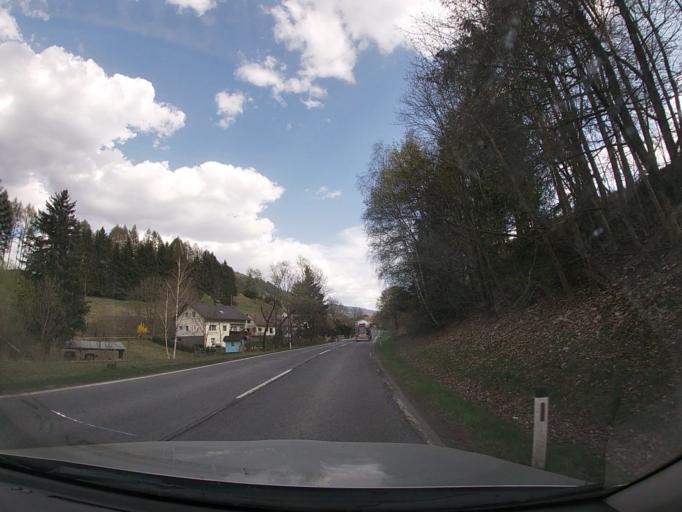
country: AT
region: Styria
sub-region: Politischer Bezirk Murau
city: Sankt Lorenzen bei Scheifling
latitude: 47.1417
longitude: 14.4212
